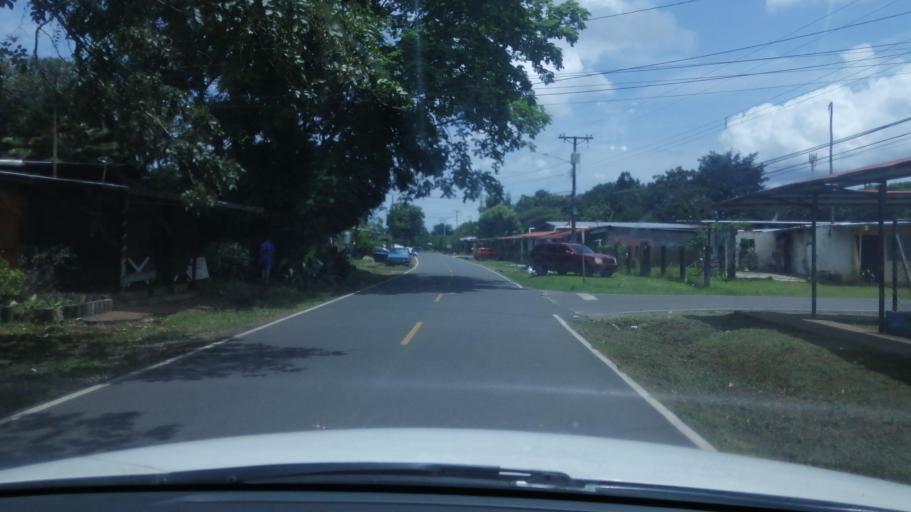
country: PA
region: Chiriqui
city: David
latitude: 8.4193
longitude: -82.4266
